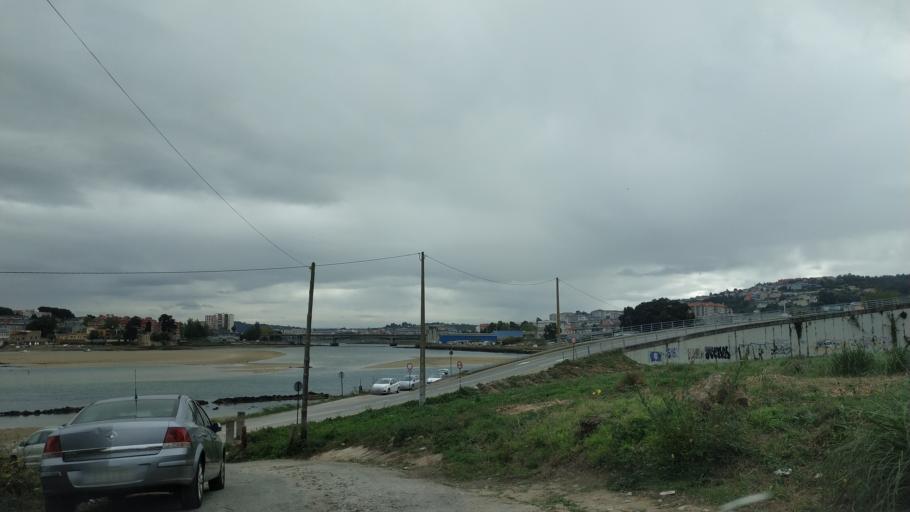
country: ES
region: Galicia
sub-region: Provincia da Coruna
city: A Coruna
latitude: 43.3387
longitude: -8.3867
